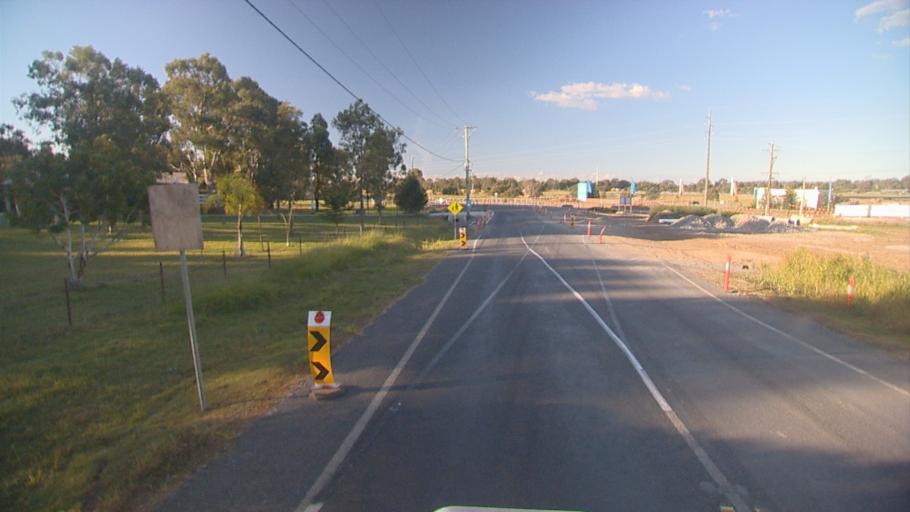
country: AU
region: Queensland
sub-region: Logan
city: Logan Reserve
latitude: -27.7177
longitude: 153.1141
